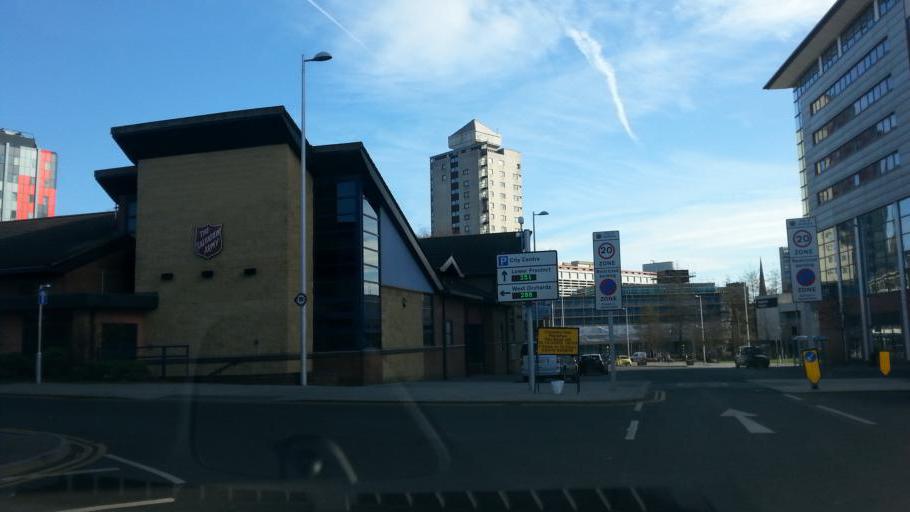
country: GB
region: England
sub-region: Coventry
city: Coventry
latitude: 52.4112
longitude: -1.5145
